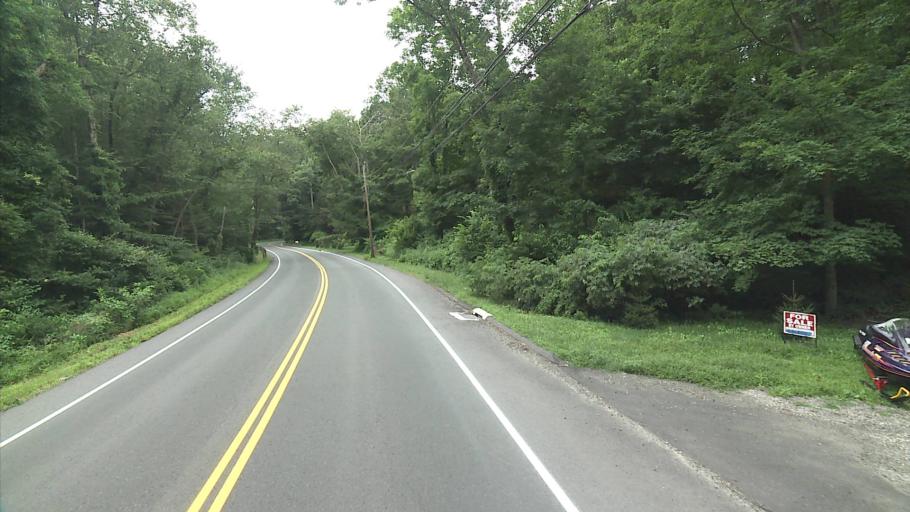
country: US
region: Connecticut
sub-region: New Haven County
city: Heritage Village
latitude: 41.5172
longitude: -73.2582
